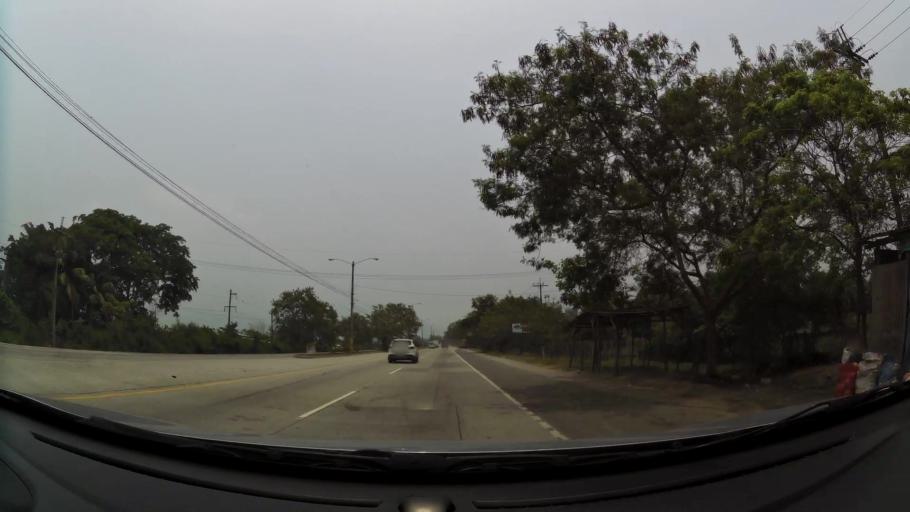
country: HN
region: Yoro
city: El Progreso
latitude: 15.4082
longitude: -87.8340
